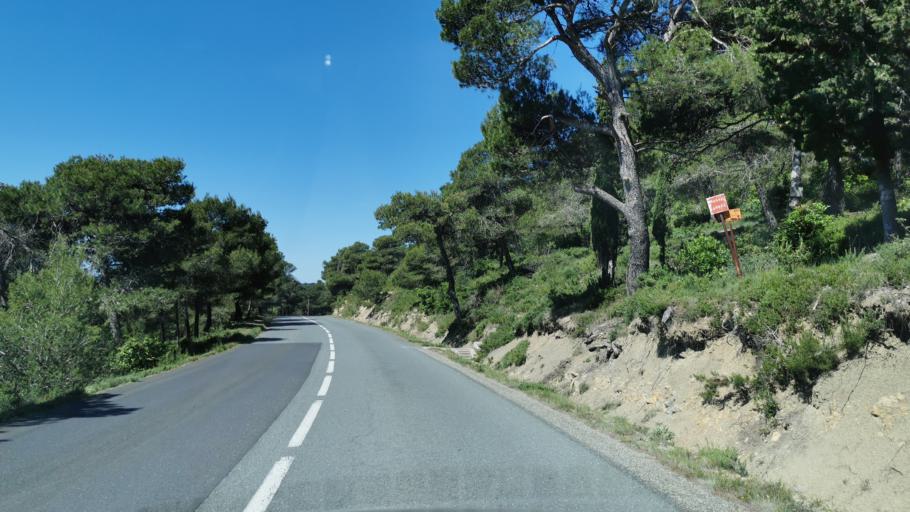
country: FR
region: Languedoc-Roussillon
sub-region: Departement de l'Aude
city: Armissan
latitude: 43.1697
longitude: 3.1204
